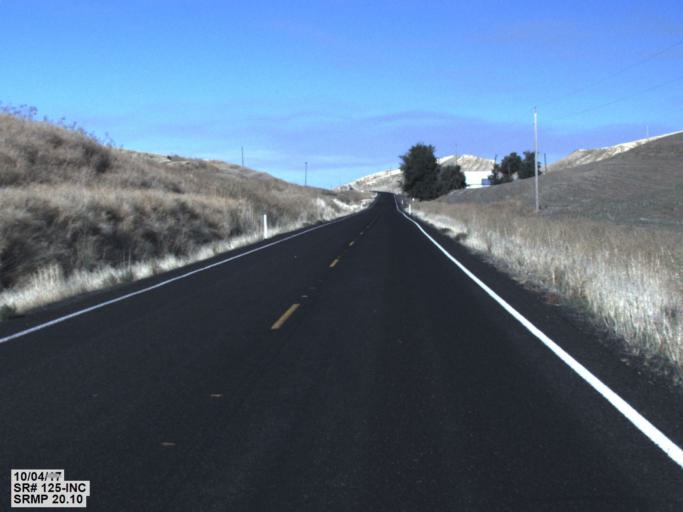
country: US
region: Washington
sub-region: Walla Walla County
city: Walla Walla
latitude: 46.2501
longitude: -118.3610
